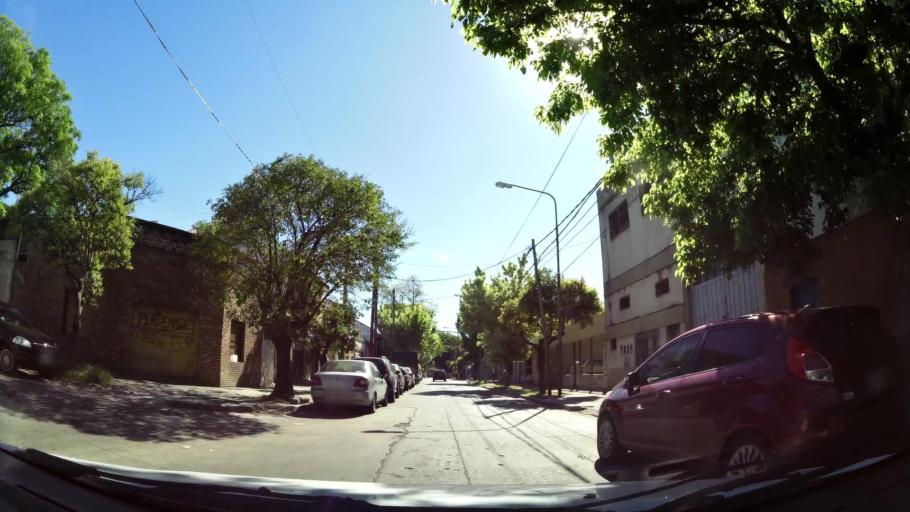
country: AR
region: Buenos Aires
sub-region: Partido de General San Martin
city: General San Martin
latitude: -34.5463
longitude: -58.5158
